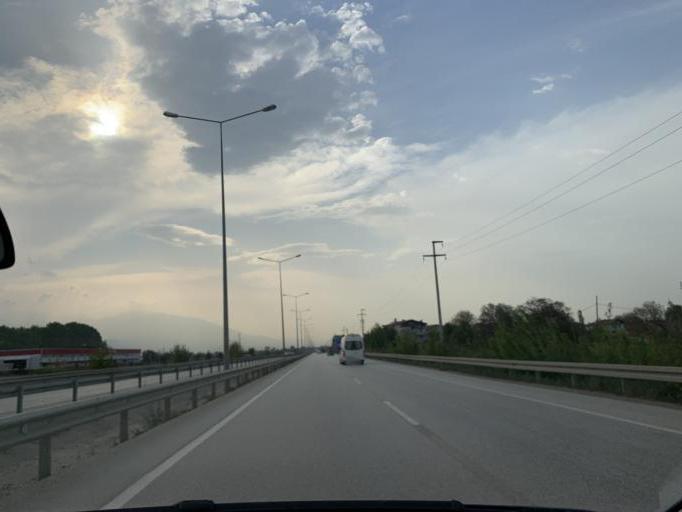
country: TR
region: Bursa
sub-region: Inegoel
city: Inegol
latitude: 40.0621
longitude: 29.5760
